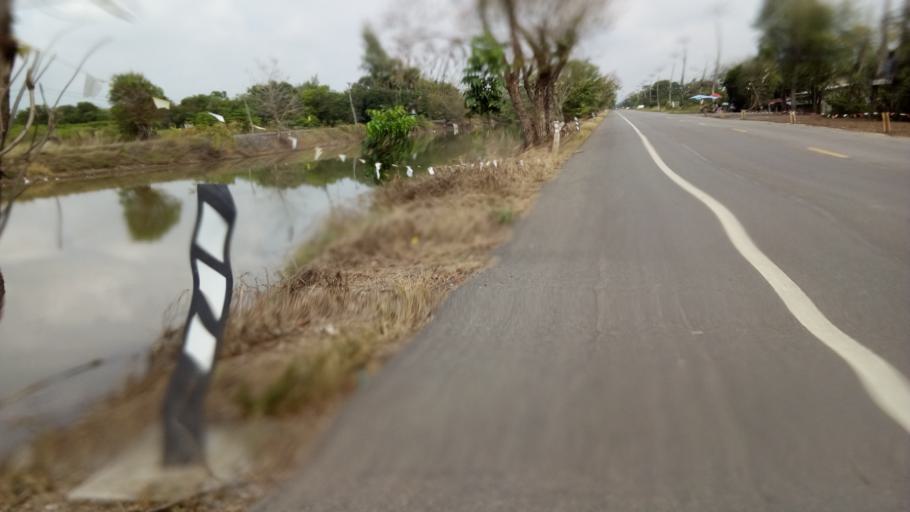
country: TH
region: Pathum Thani
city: Nong Suea
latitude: 14.1770
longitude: 100.8236
